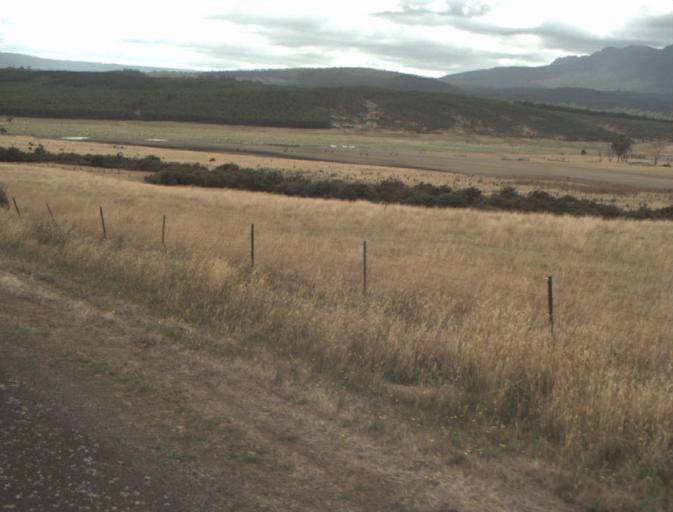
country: AU
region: Tasmania
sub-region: Northern Midlands
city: Evandale
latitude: -41.5099
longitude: 147.4789
